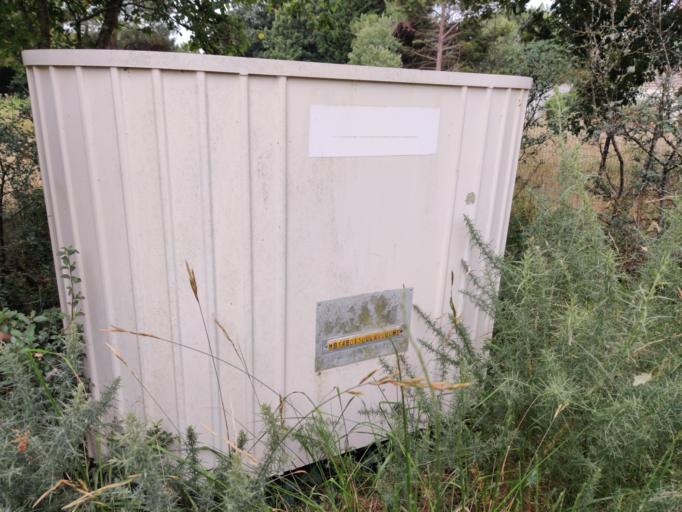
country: FR
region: Pays de la Loire
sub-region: Departement de la Vendee
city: Vaire
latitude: 46.5966
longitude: -1.8115
